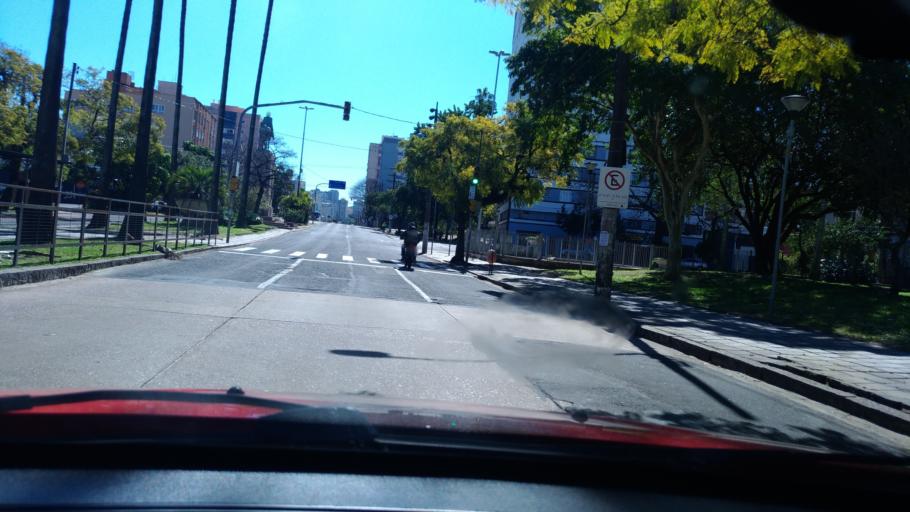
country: BR
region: Rio Grande do Sul
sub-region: Porto Alegre
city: Porto Alegre
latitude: -30.0447
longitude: -51.2136
